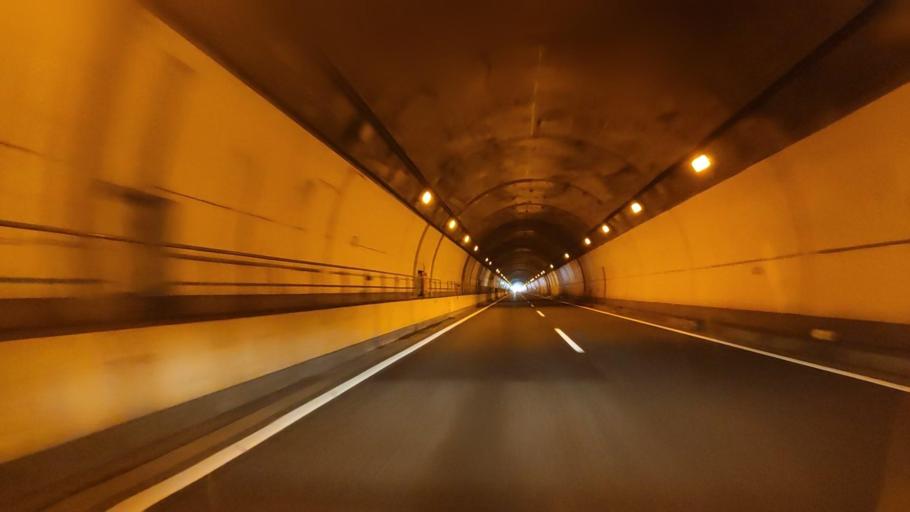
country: JP
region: Akita
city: Hanawa
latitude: 40.0105
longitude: 140.9884
